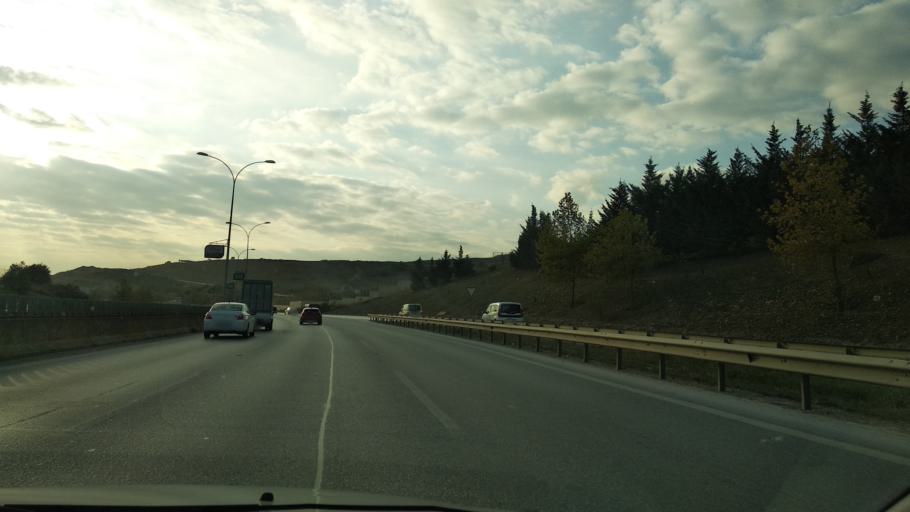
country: TR
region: Istanbul
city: Icmeler
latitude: 40.8775
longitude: 29.3074
